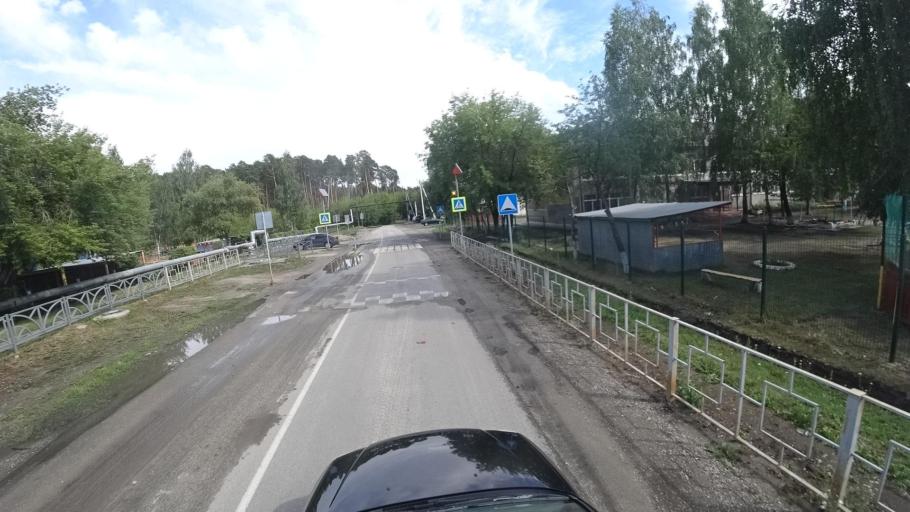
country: RU
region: Sverdlovsk
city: Kamyshlov
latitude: 56.8353
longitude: 62.7329
